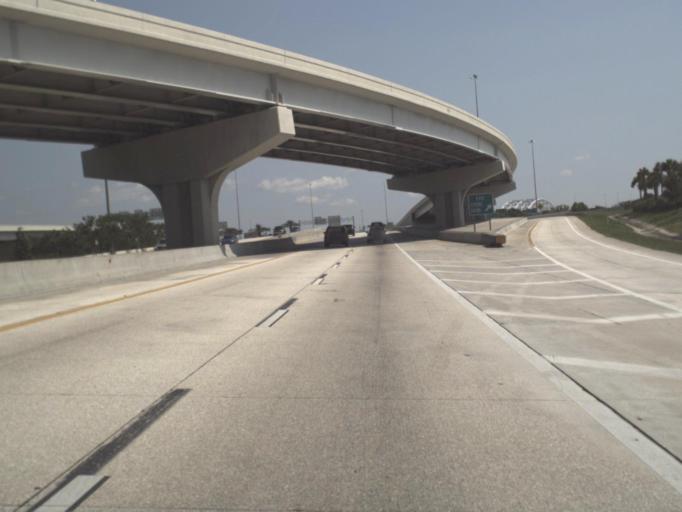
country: US
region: Florida
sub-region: Duval County
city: Jacksonville
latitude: 30.3214
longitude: -81.6813
